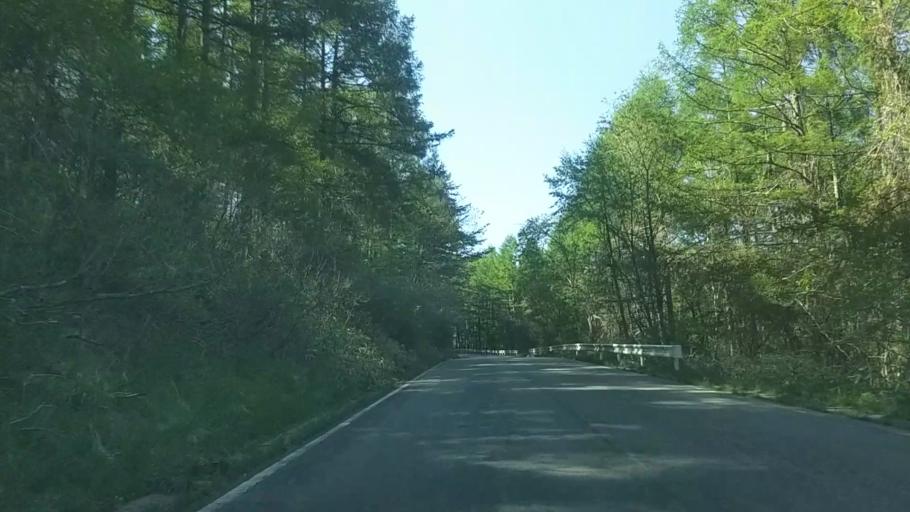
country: JP
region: Yamanashi
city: Nirasaki
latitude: 35.9200
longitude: 138.4026
